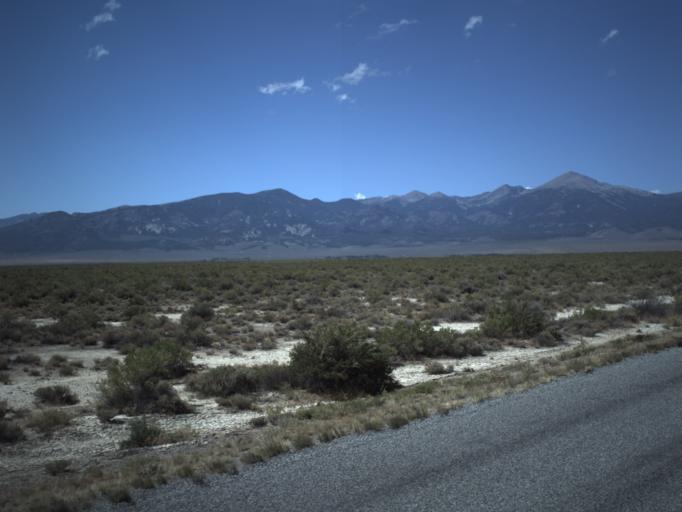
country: US
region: Nevada
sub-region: White Pine County
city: McGill
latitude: 39.0556
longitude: -114.0292
